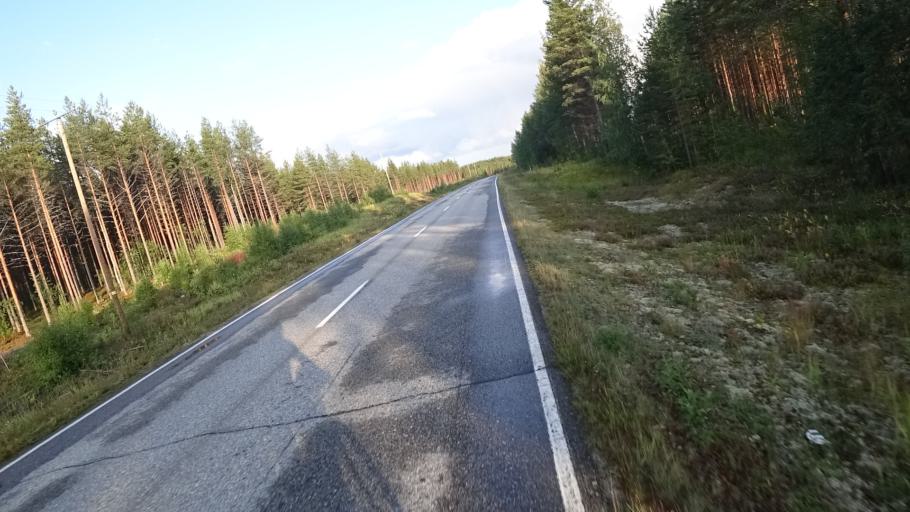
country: FI
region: North Karelia
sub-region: Joensuu
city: Ilomantsi
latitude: 62.6381
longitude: 31.0836
